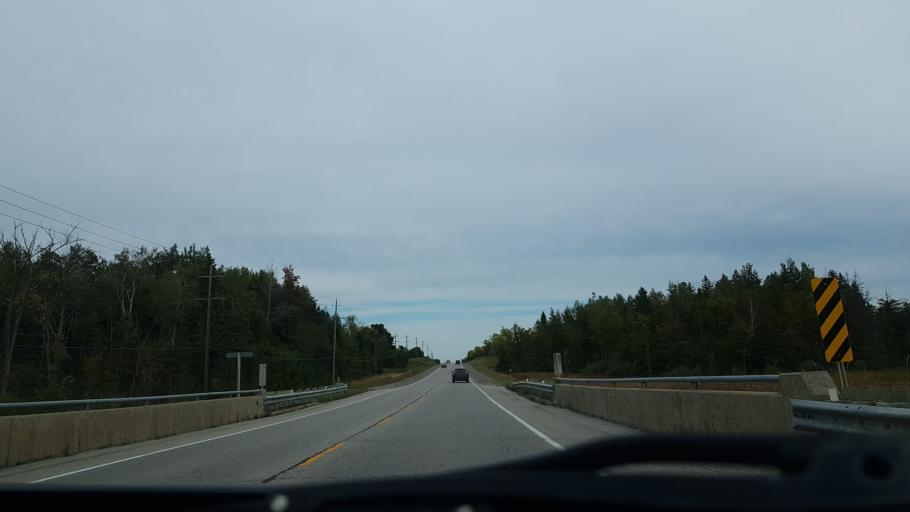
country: CA
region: Ontario
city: Orangeville
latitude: 43.7950
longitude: -80.0678
